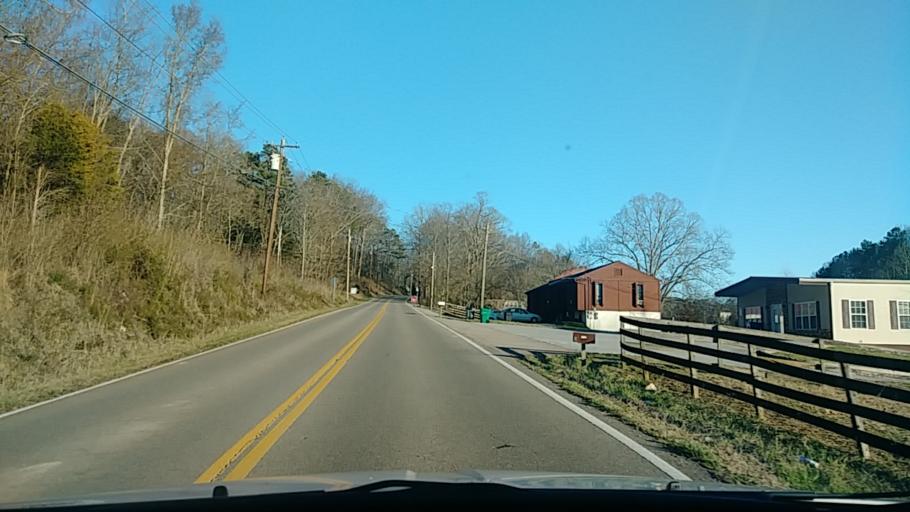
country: US
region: Tennessee
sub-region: Hamblen County
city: Morristown
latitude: 36.1945
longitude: -83.3926
